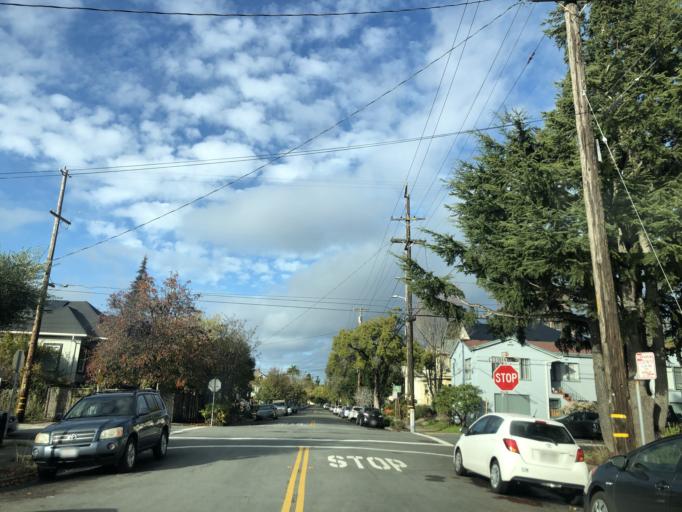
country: US
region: California
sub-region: Alameda County
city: Berkeley
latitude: 37.8525
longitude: -122.2618
